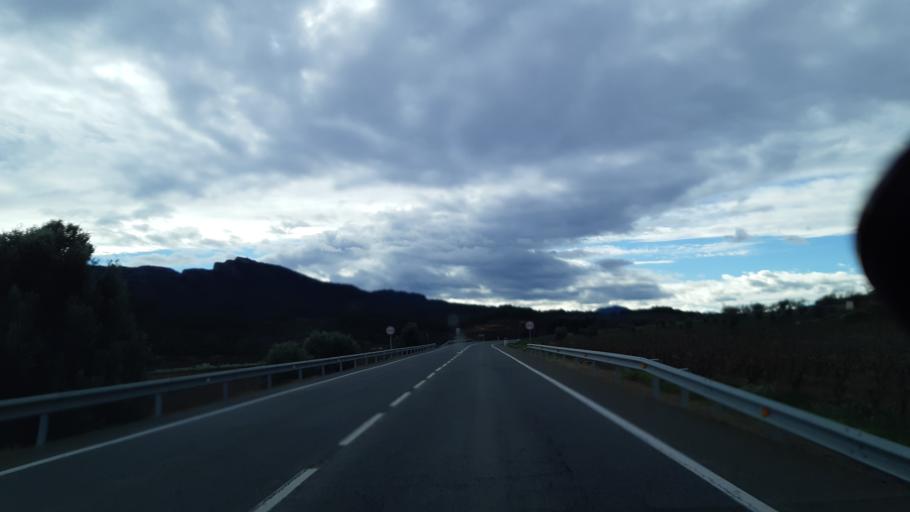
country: ES
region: Catalonia
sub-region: Provincia de Tarragona
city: Gandesa
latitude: 41.0883
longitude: 0.5118
